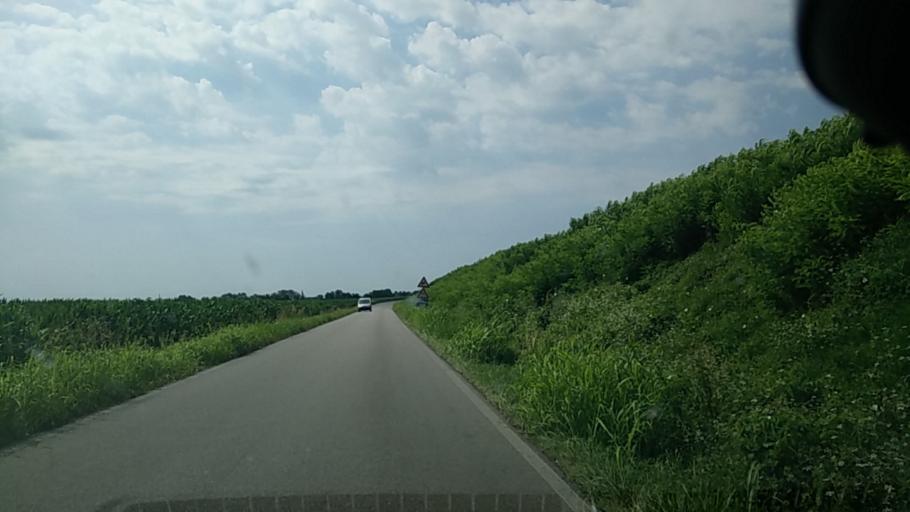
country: IT
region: Friuli Venezia Giulia
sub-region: Provincia di Pordenone
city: Puia-Villanova
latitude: 45.8328
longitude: 12.5733
